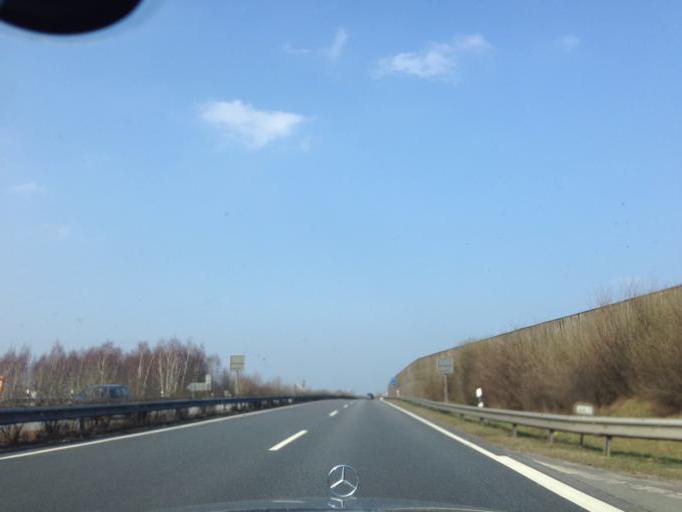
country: DE
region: Schleswig-Holstein
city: Hogersdorf
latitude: 53.9177
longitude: 10.2740
